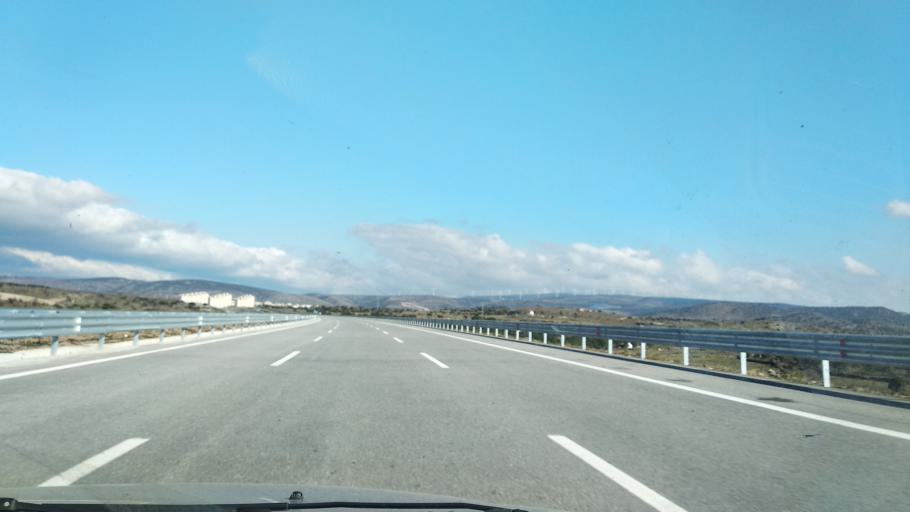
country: TR
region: Izmir
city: Yenisakran
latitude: 38.8644
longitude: 27.0790
